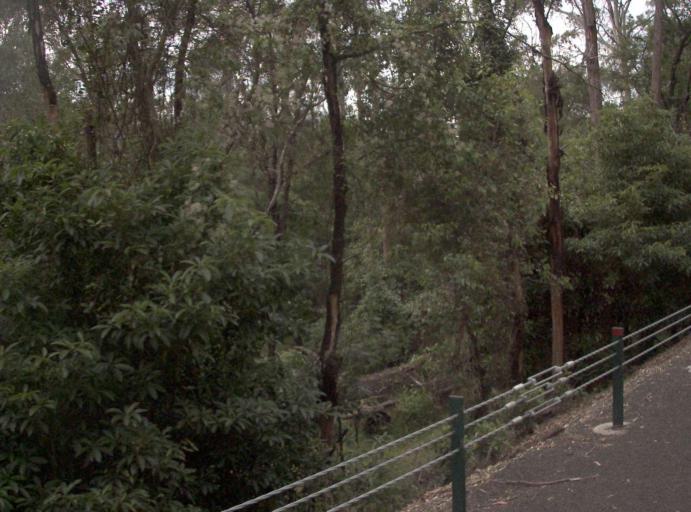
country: AU
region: New South Wales
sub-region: Bombala
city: Bombala
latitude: -37.4686
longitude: 149.1793
